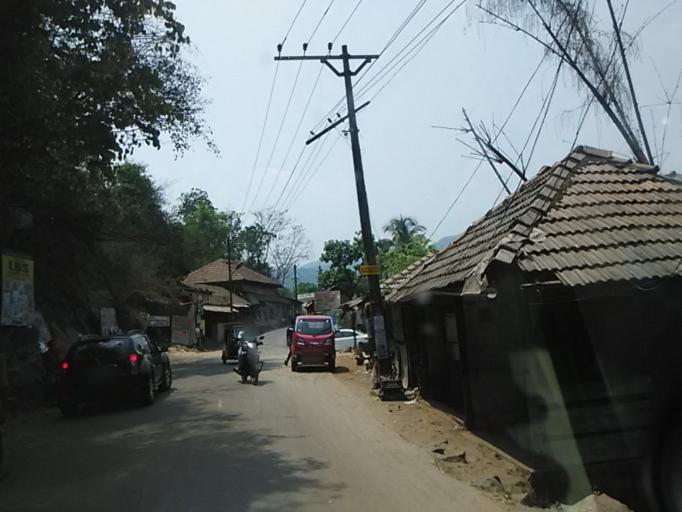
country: IN
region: Karnataka
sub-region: Kodagu
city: Virarajendrapet
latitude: 12.0697
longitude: 75.7176
